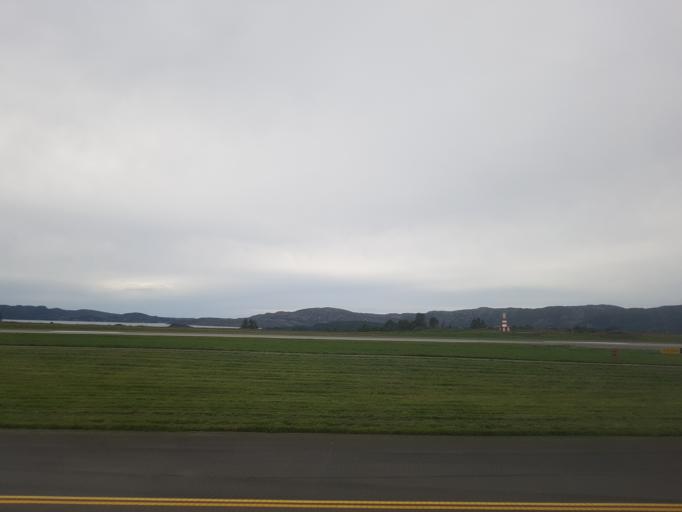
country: NO
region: Hordaland
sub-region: Bergen
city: Ytrebygda
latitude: 60.3000
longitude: 5.2191
